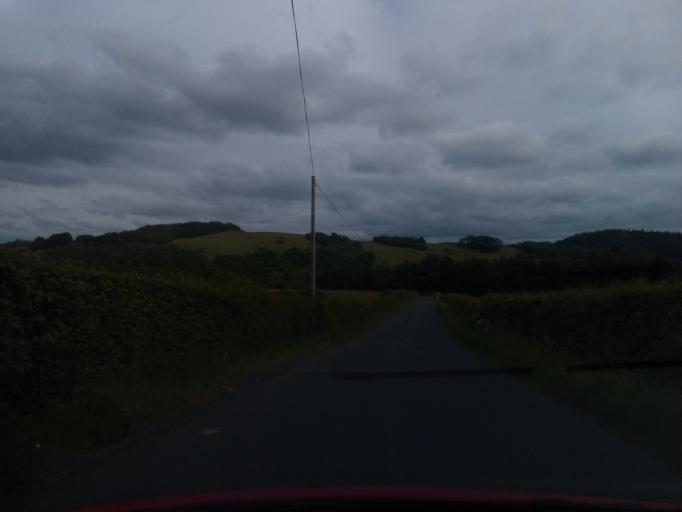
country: GB
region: Scotland
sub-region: The Scottish Borders
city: Galashiels
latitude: 55.5820
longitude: -2.8195
